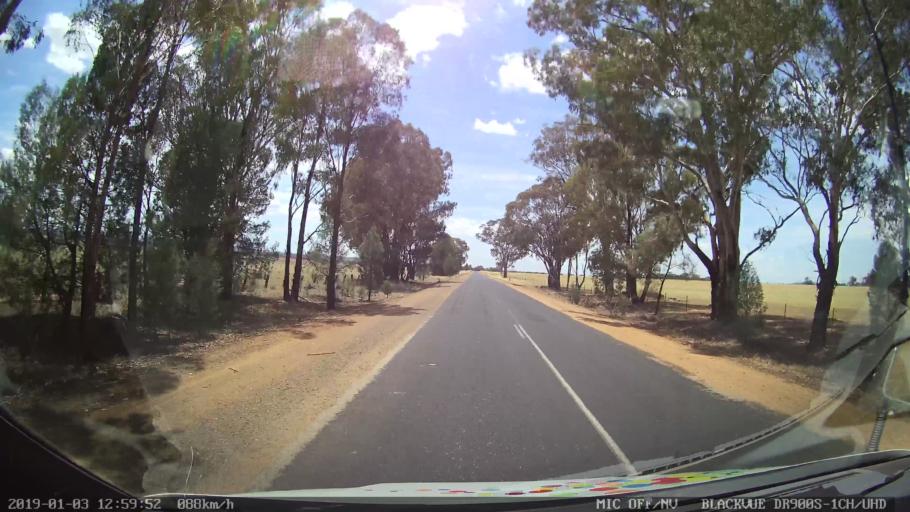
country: AU
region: New South Wales
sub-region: Cabonne
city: Canowindra
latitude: -33.6339
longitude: 148.3952
